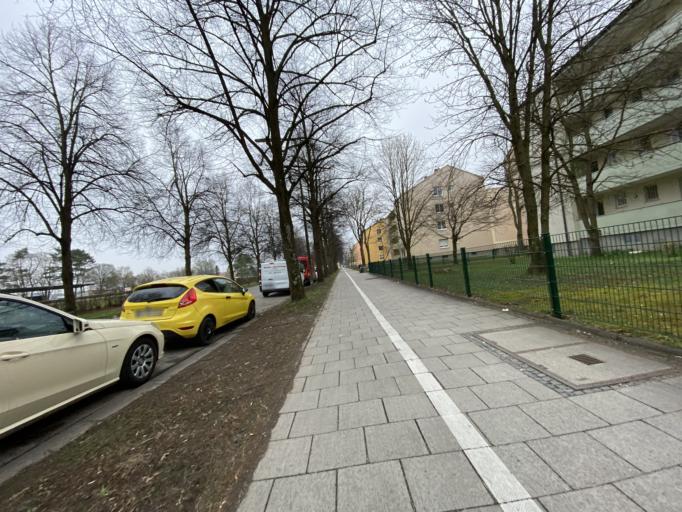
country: DE
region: Bavaria
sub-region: Upper Bavaria
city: Oberschleissheim
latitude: 48.2193
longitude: 11.5612
